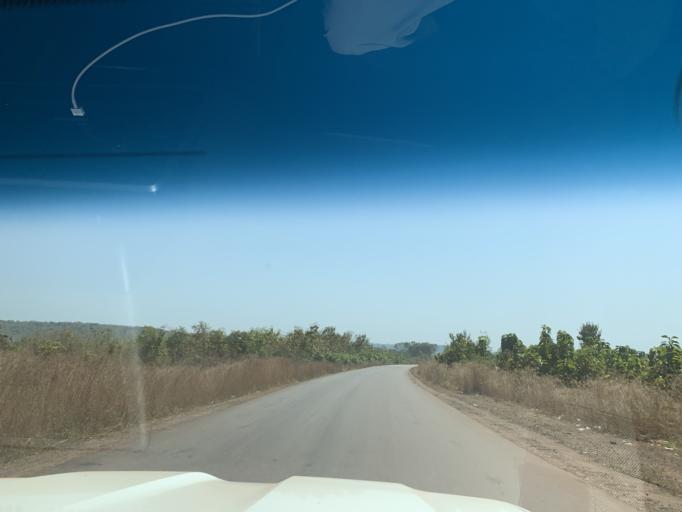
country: GN
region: Kindia
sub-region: Kindia
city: Kindia
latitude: 10.0008
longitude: -12.7600
